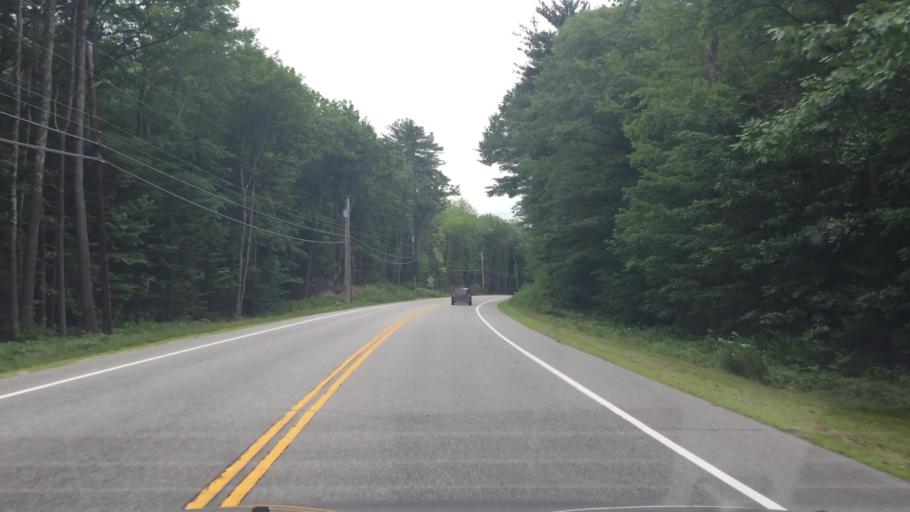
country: US
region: New Hampshire
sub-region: Carroll County
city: Sandwich
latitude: 43.7984
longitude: -71.3688
